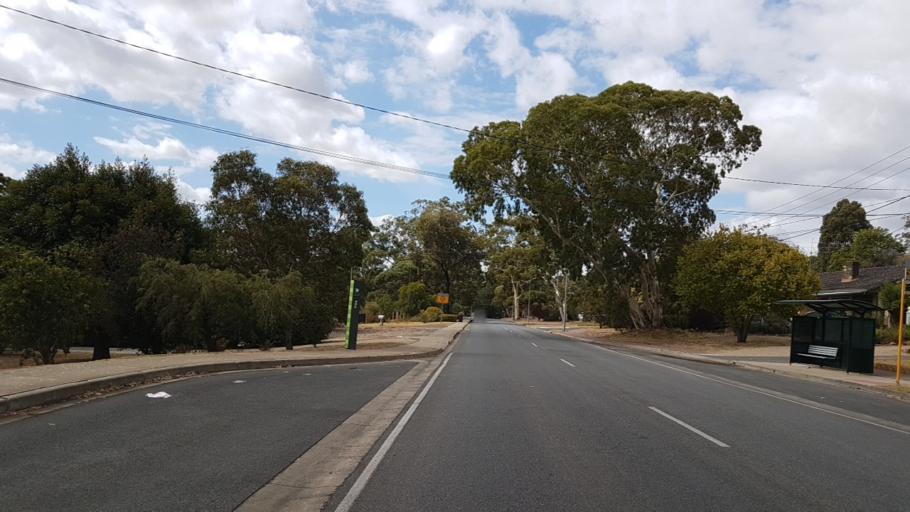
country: AU
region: South Australia
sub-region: Tea Tree Gully
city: Hope Valley
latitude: -34.8398
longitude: 138.7228
